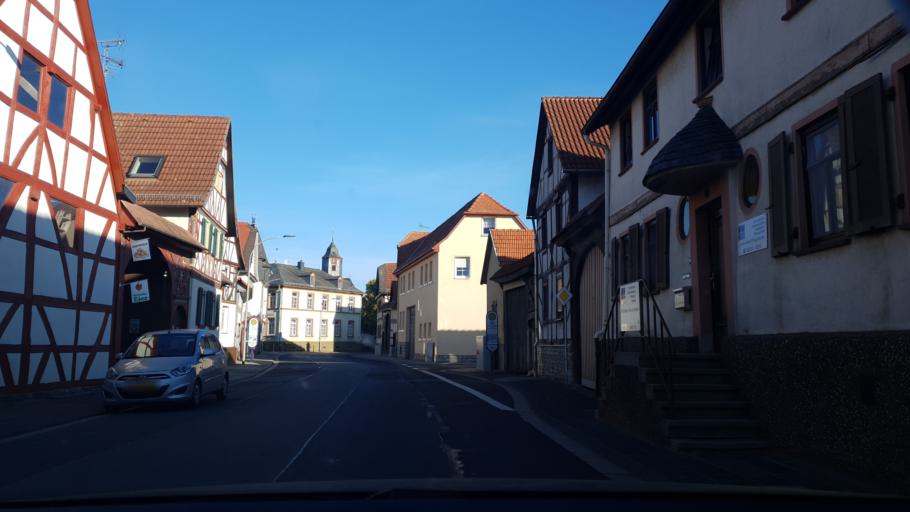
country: DE
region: Hesse
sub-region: Regierungsbezirk Darmstadt
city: Butzbach
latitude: 50.4608
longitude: 8.6515
